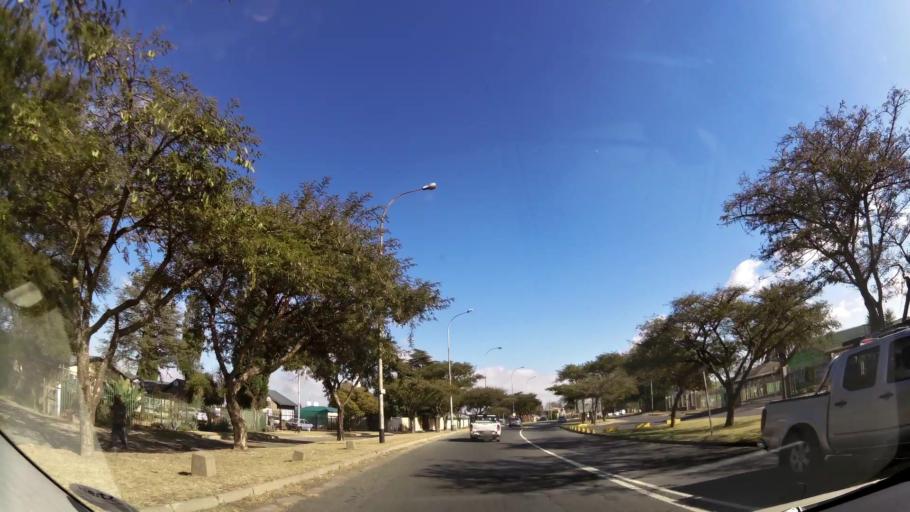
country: ZA
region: Gauteng
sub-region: City of Johannesburg Metropolitan Municipality
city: Roodepoort
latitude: -26.1325
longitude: 27.8371
